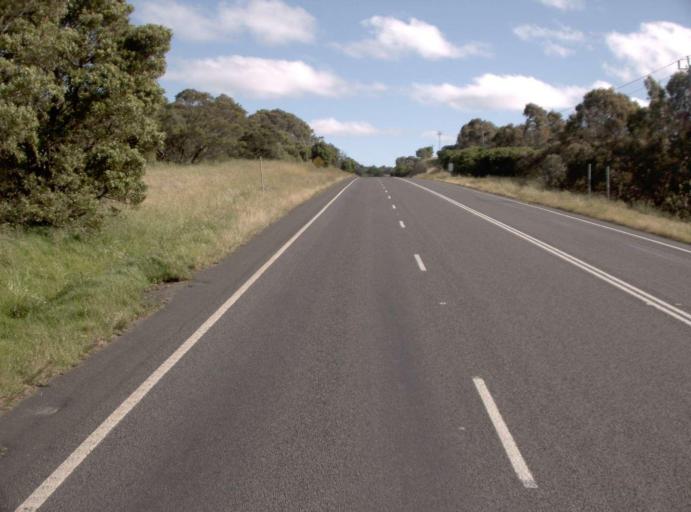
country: AU
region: Victoria
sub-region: Bass Coast
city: North Wonthaggi
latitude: -38.5135
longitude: 145.4493
